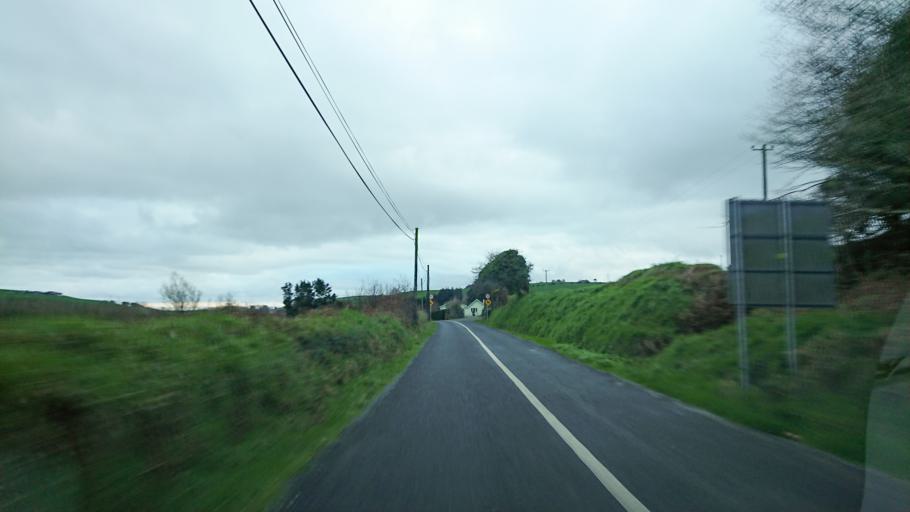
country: IE
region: Munster
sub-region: Waterford
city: Portlaw
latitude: 52.1575
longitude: -7.3841
